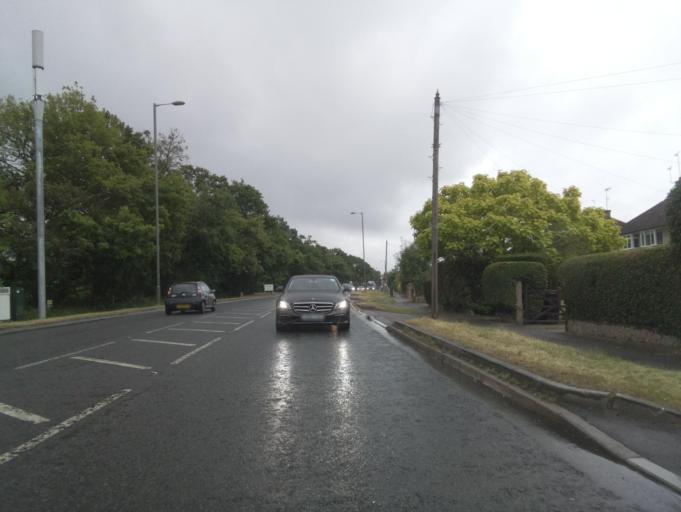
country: GB
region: England
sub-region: Surrey
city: Salfords
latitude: 51.1966
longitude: -0.1643
